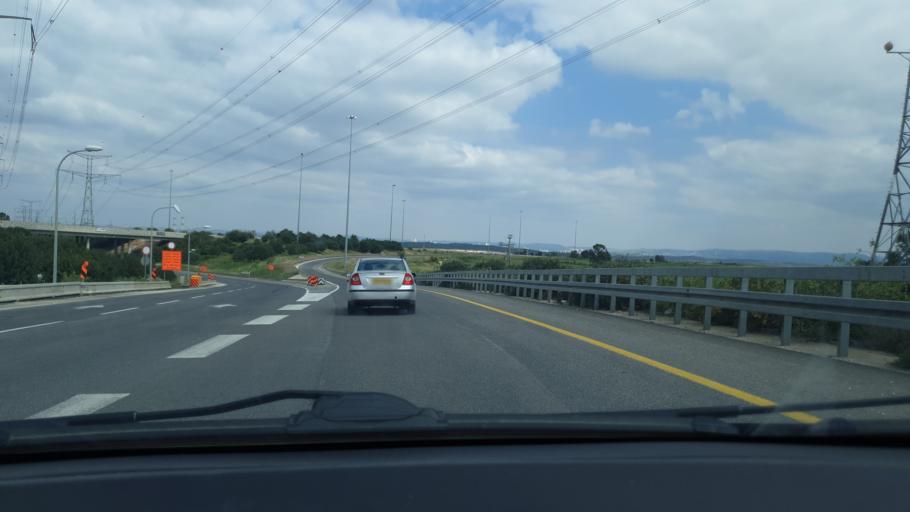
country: IL
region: Central District
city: Ramla
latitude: 31.9087
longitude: 34.8969
